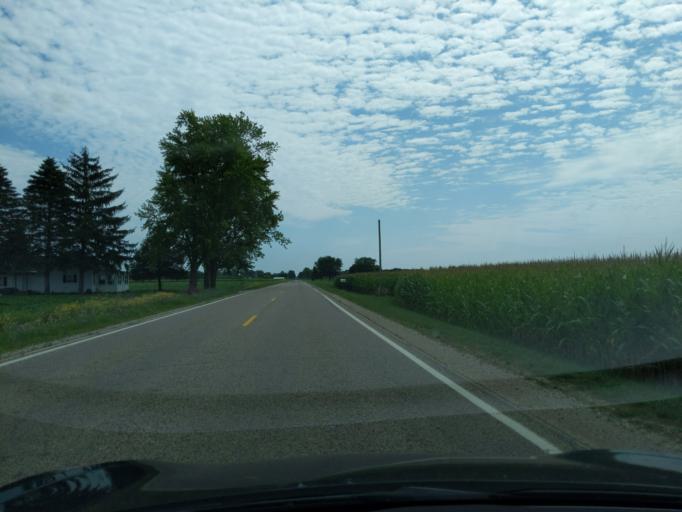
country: US
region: Michigan
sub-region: Gratiot County
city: Breckenridge
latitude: 43.2918
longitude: -84.4453
